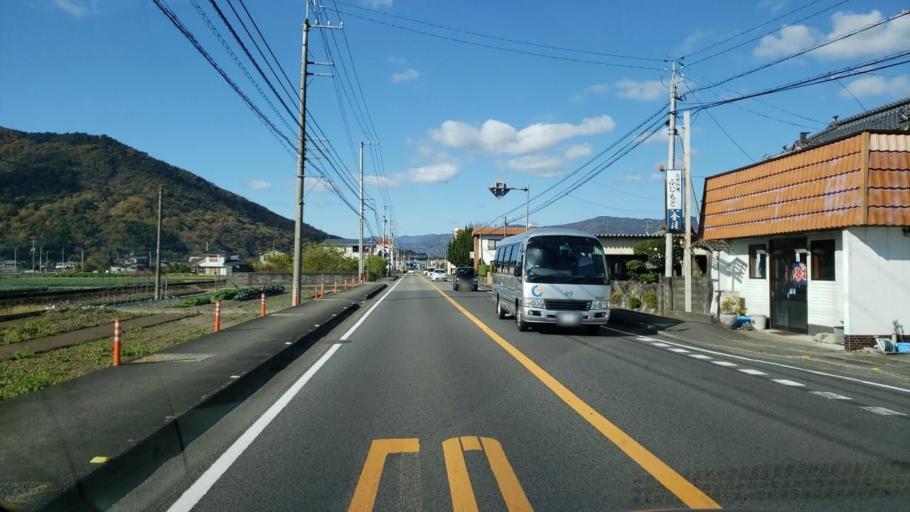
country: JP
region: Tokushima
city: Wakimachi
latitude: 34.0602
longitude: 134.2137
